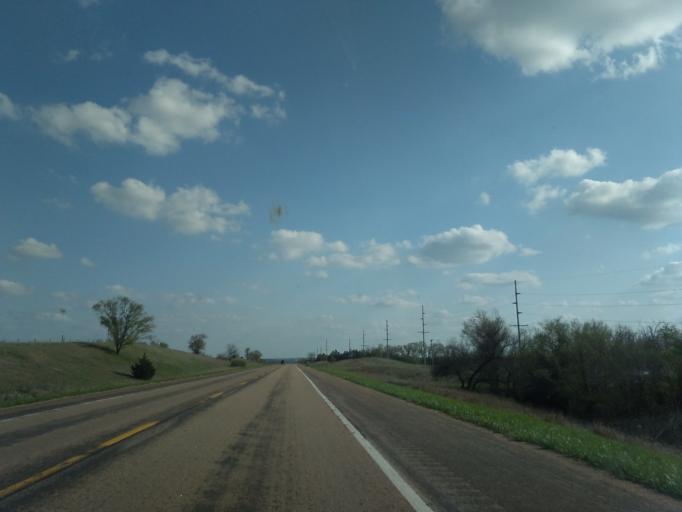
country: US
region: Nebraska
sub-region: Webster County
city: Red Cloud
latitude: 40.1144
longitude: -98.5189
